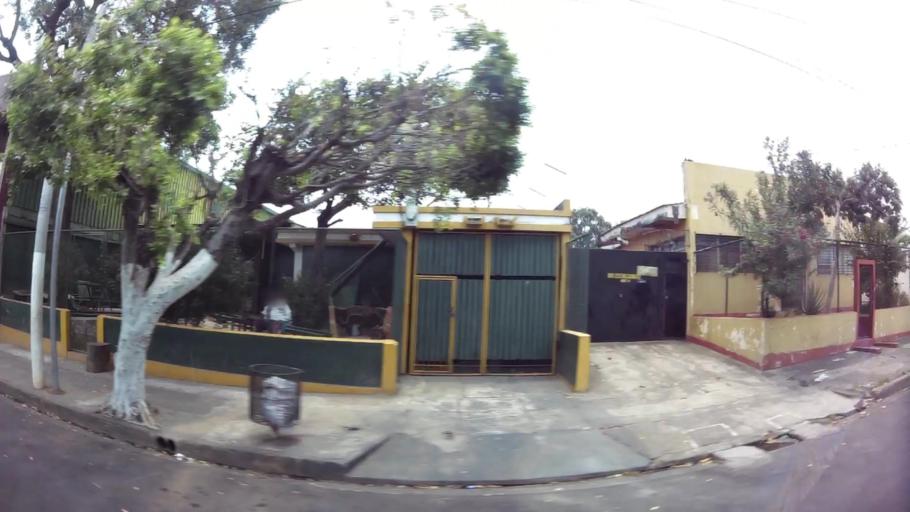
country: NI
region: Managua
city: Managua
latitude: 12.1367
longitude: -86.2926
